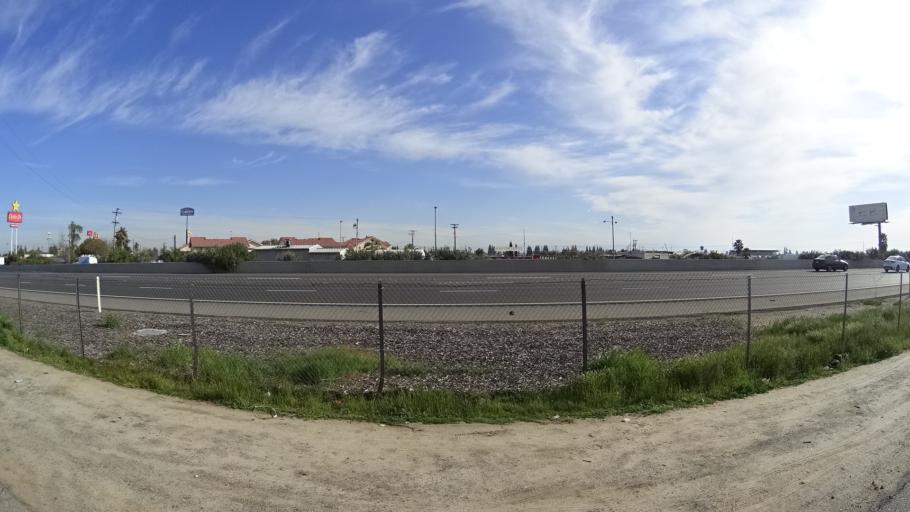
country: US
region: California
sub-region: Fresno County
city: West Park
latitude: 36.8054
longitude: -119.8837
